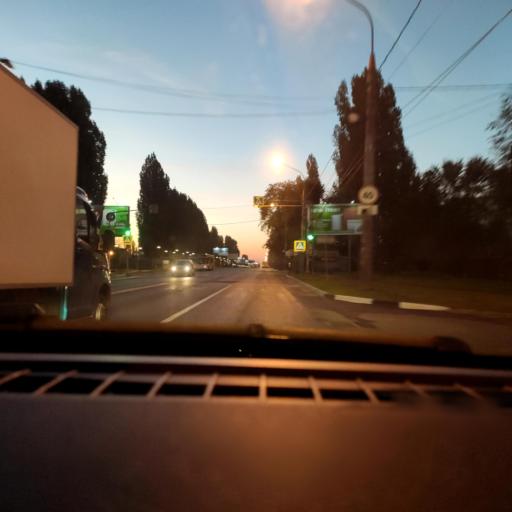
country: RU
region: Voronezj
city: Voronezh
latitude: 51.6700
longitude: 39.2583
